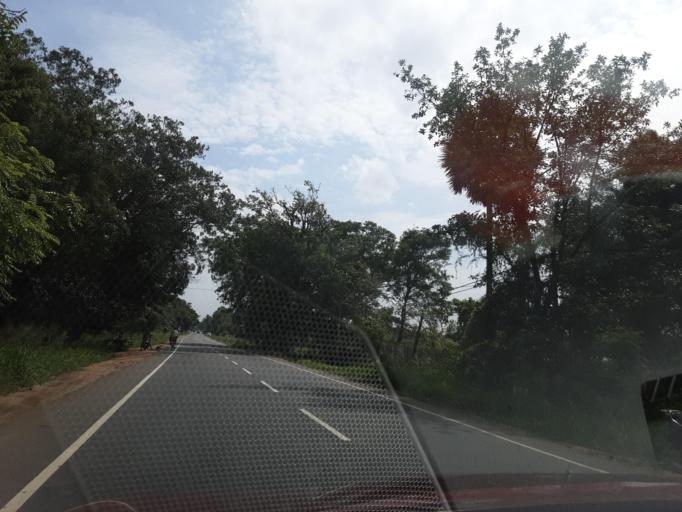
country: LK
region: Northern Province
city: Vavuniya
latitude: 8.5278
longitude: 80.4990
